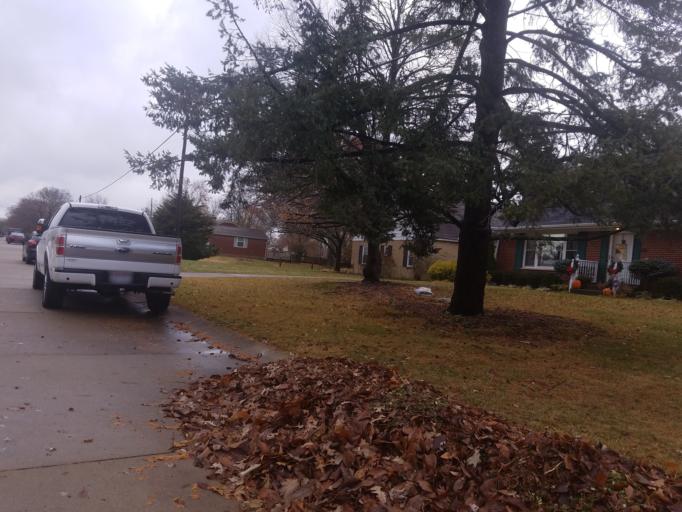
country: US
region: Ohio
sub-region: Montgomery County
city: Kettering
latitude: 39.7053
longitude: -84.1562
